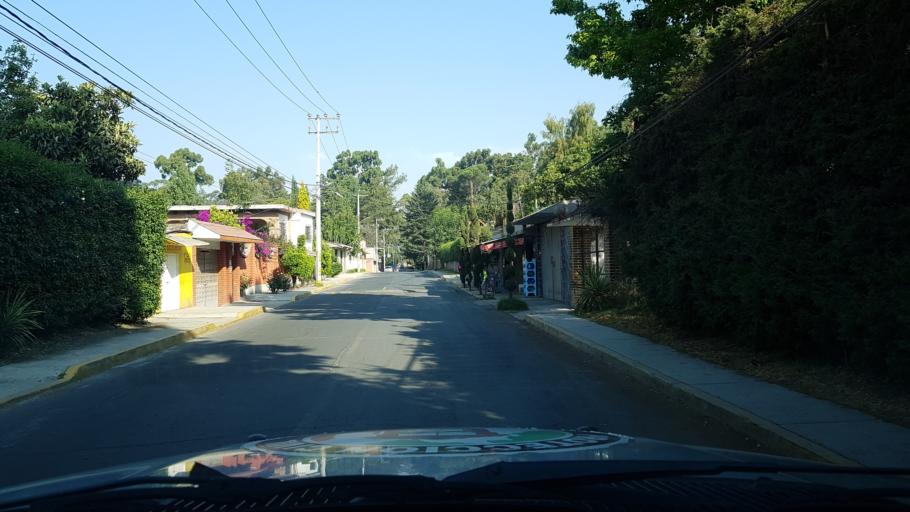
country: MX
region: Mexico
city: Ozumba de Alzate
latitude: 19.0577
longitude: -98.7760
